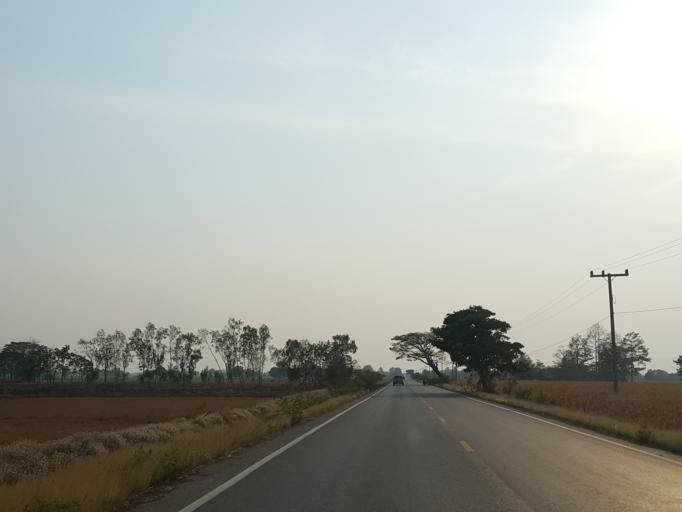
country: TH
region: Uttaradit
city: Phichai
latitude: 17.1983
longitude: 100.0283
